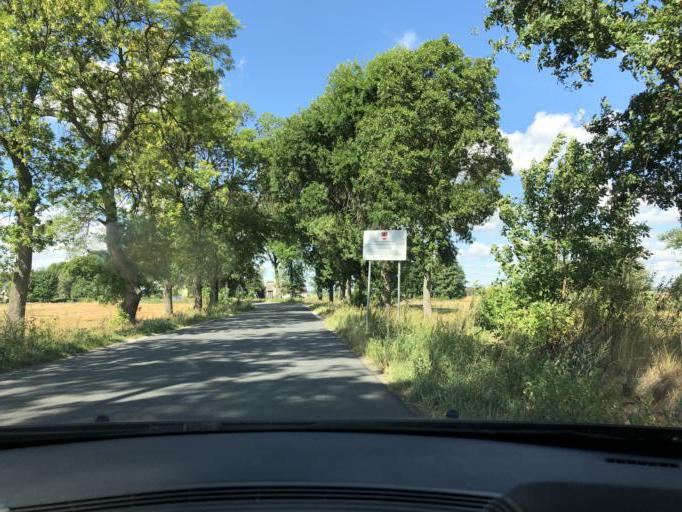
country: PL
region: Lodz Voivodeship
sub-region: Powiat wieruszowski
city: Czastary
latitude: 51.2420
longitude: 18.3646
